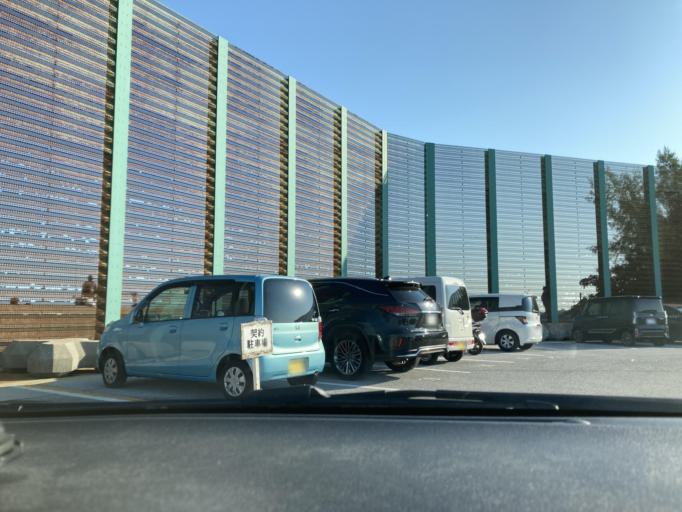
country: JP
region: Okinawa
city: Naha-shi
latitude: 26.2206
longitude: 127.6628
